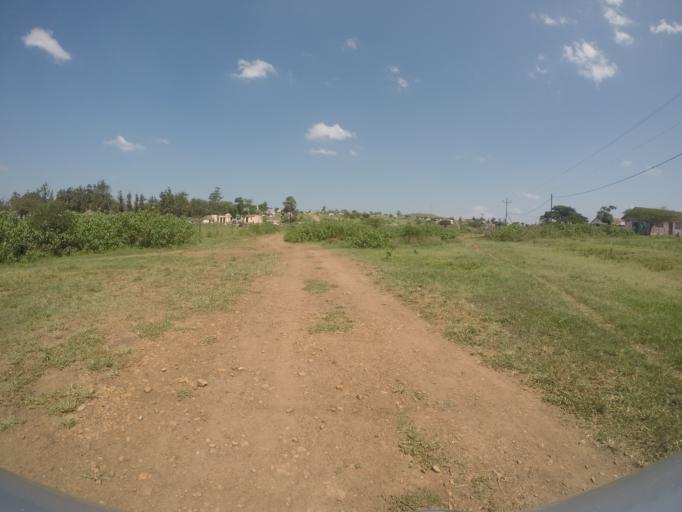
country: ZA
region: KwaZulu-Natal
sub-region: uThungulu District Municipality
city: Empangeni
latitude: -28.5881
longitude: 31.7404
